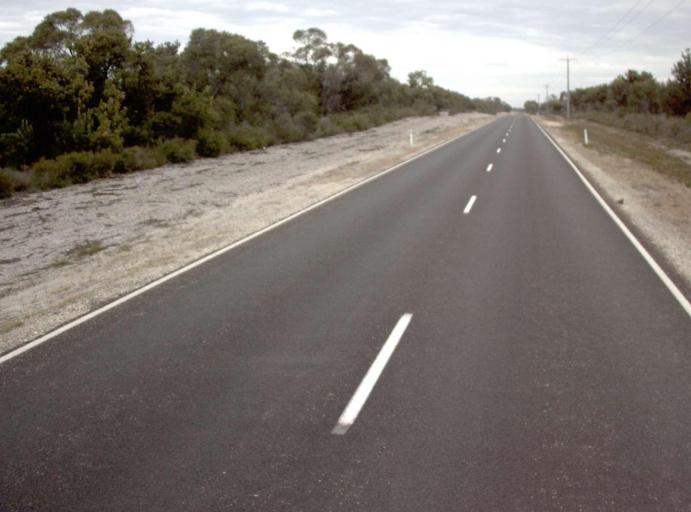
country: AU
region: Victoria
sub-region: Wellington
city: Sale
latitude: -38.1700
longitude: 147.3850
